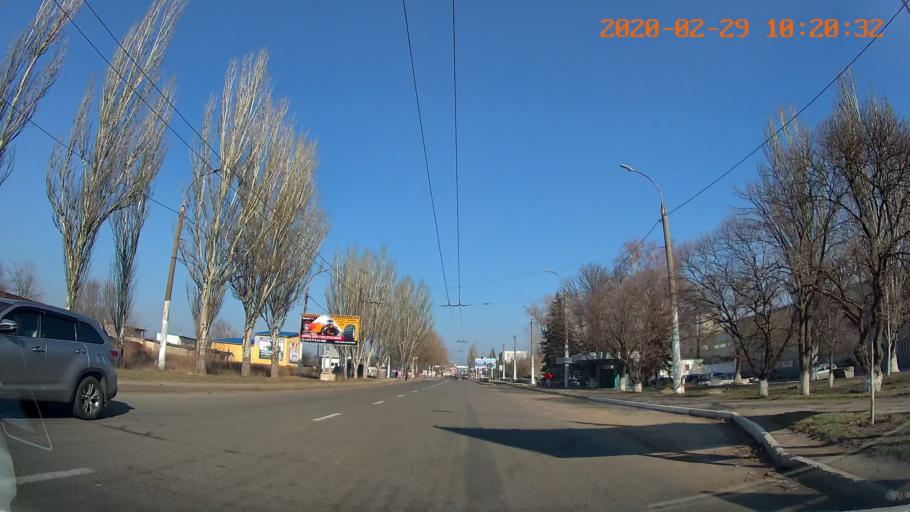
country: MD
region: Telenesti
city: Tiraspolul Nou
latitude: 46.8612
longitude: 29.6104
